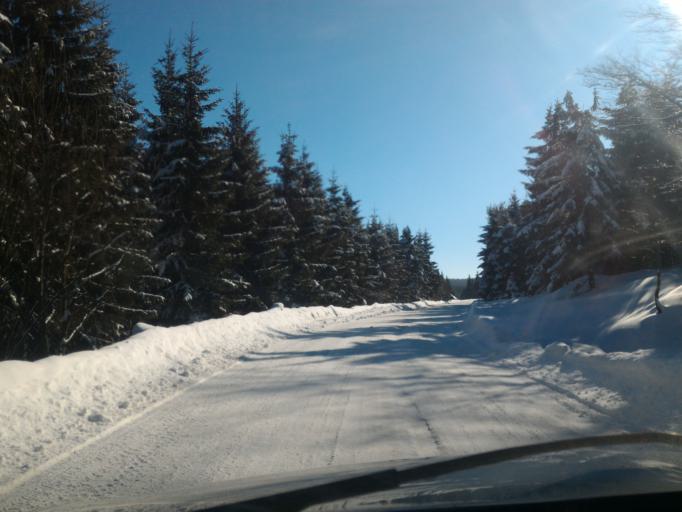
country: CZ
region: Liberecky
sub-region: Okres Jablonec nad Nisou
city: Josefuv Dul
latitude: 50.8453
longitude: 15.2705
